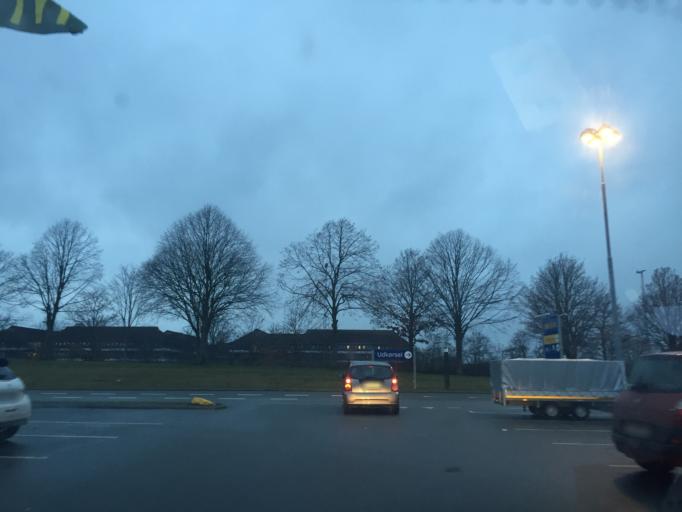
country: DK
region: Capital Region
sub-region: Hoje-Taastrup Kommune
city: Taastrup
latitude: 55.6592
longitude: 12.2841
